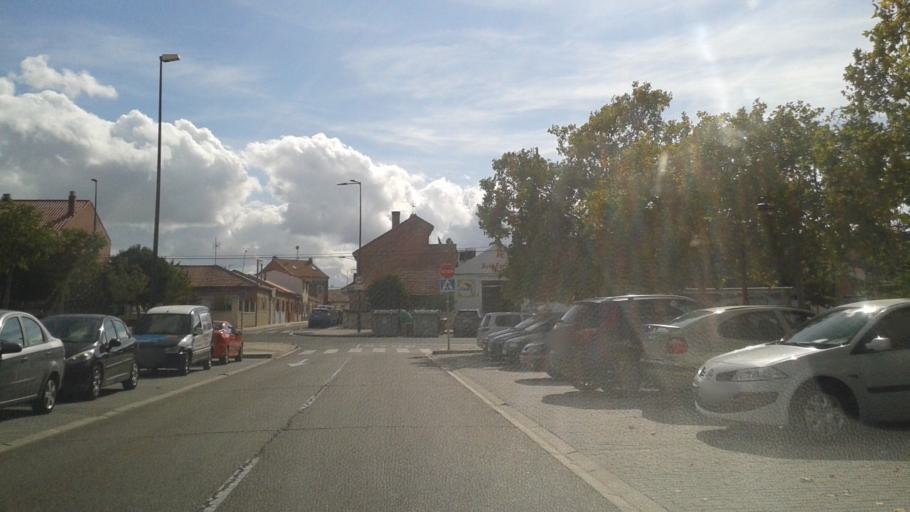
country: ES
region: Castille and Leon
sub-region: Provincia de Valladolid
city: Valladolid
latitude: 41.6600
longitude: -4.7064
